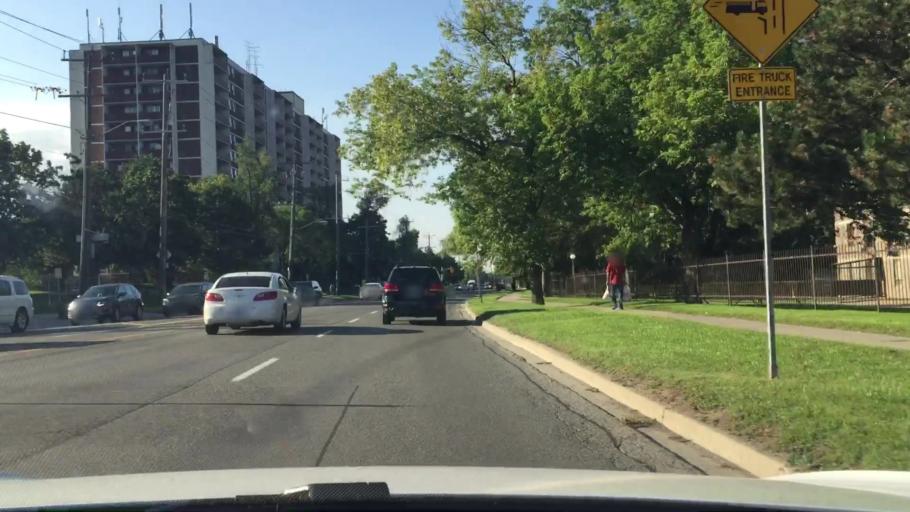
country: CA
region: Ontario
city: Scarborough
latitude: 43.7816
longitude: -79.2983
